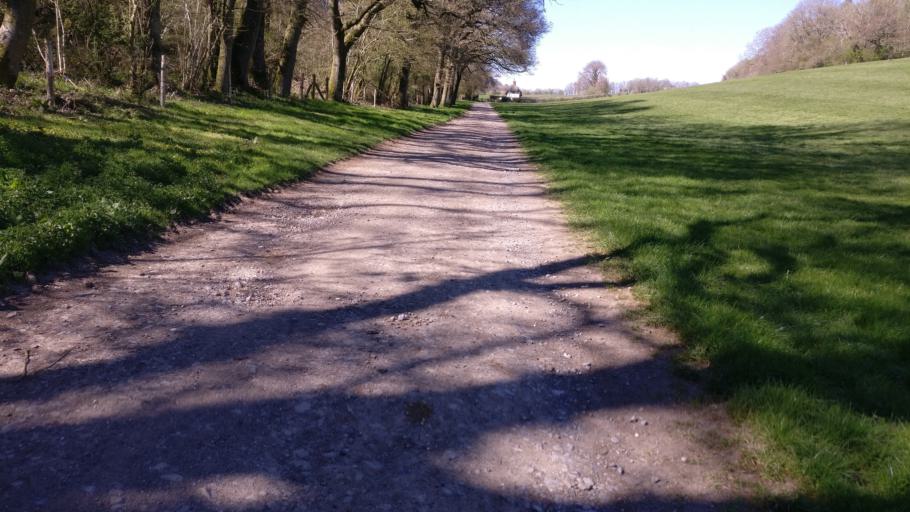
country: GB
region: England
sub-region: Hampshire
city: Basingstoke
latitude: 51.2098
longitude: -1.1051
